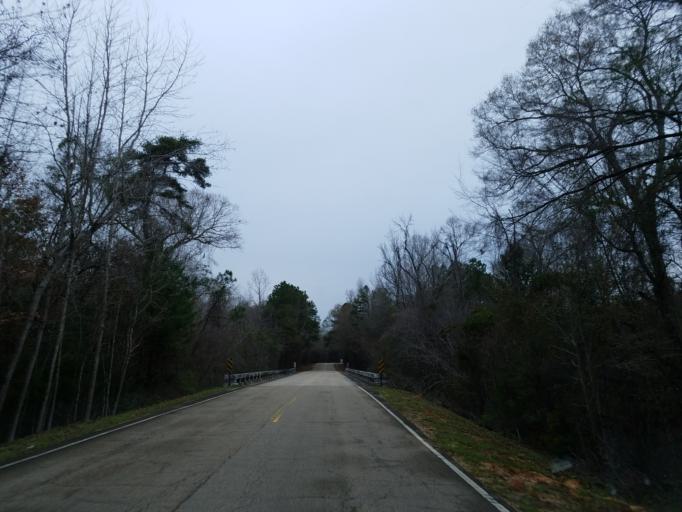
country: US
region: Mississippi
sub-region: Forrest County
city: Hattiesburg
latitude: 31.2513
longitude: -89.2308
